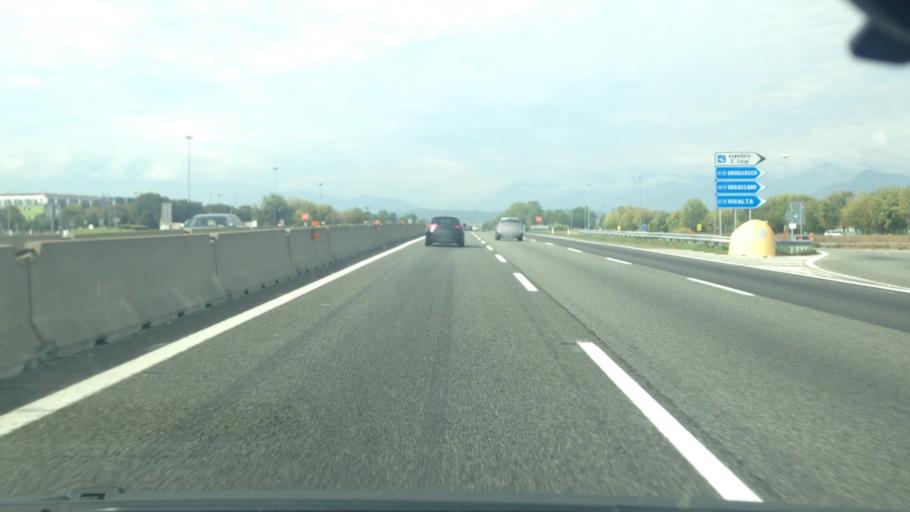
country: IT
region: Piedmont
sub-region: Provincia di Torino
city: Beinasco
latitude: 45.0378
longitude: 7.5689
